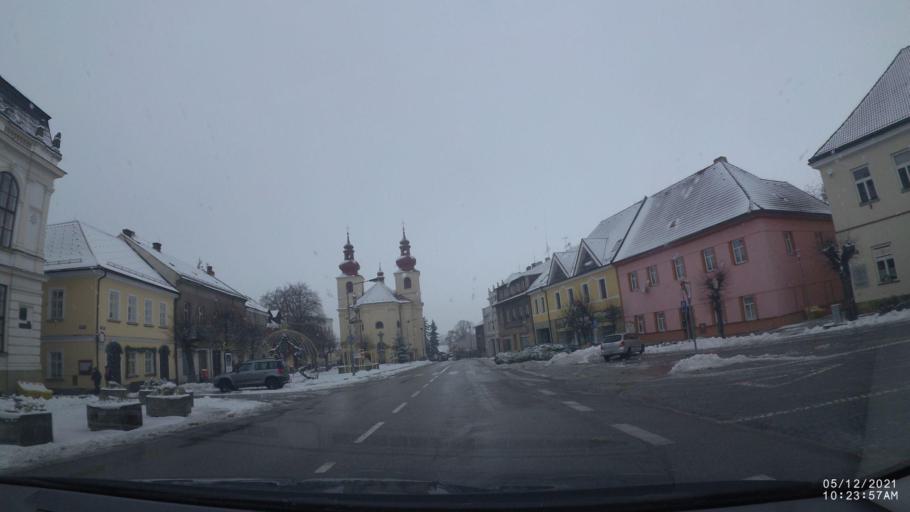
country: CZ
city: Vamberk
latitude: 50.1177
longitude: 16.2897
